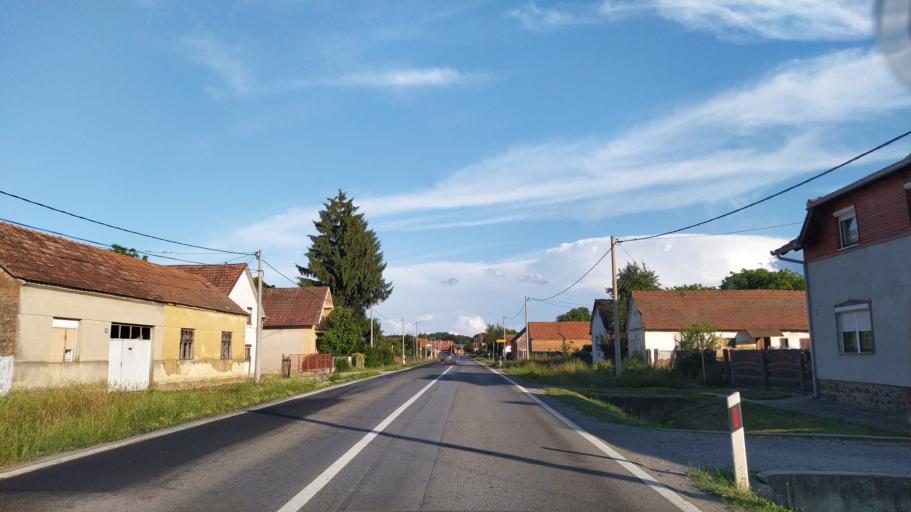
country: HR
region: Virovitick-Podravska
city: Slatina
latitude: 45.6810
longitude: 17.7441
